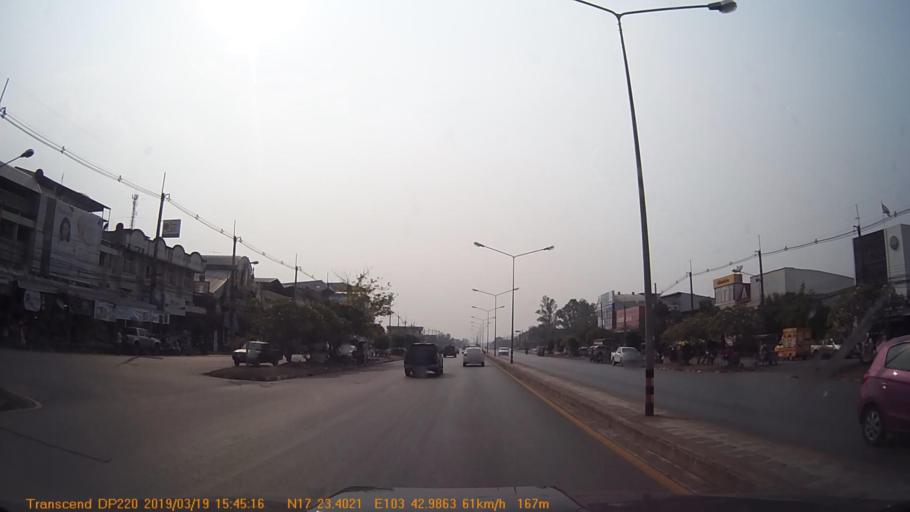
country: TH
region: Sakon Nakhon
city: Phang Khon
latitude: 17.3901
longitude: 103.7163
